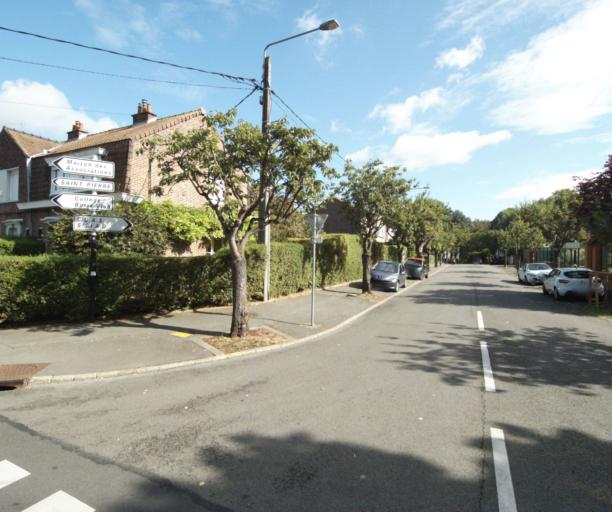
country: FR
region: Nord-Pas-de-Calais
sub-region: Departement du Nord
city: Croix
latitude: 50.6813
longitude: 3.1535
